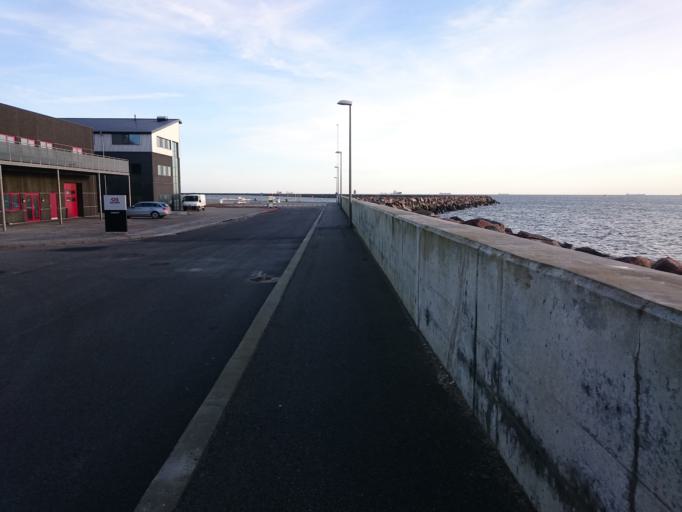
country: DK
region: North Denmark
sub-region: Frederikshavn Kommune
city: Skagen
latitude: 57.7132
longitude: 10.5814
